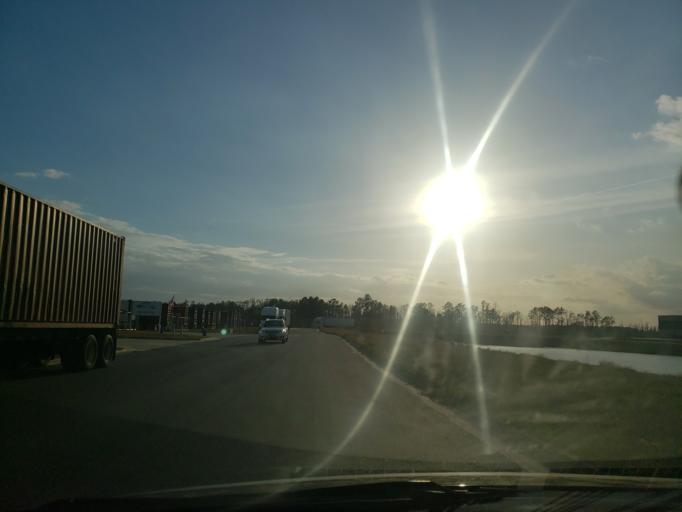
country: US
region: Georgia
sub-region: Chatham County
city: Bloomingdale
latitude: 32.1604
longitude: -81.2726
